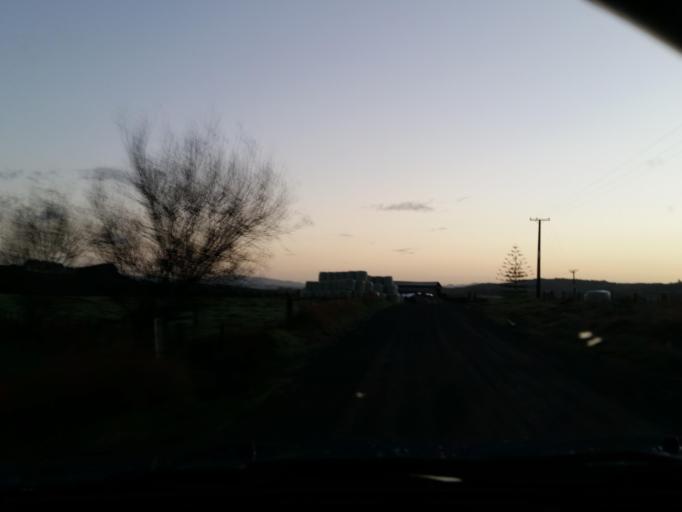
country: NZ
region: Northland
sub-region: Whangarei
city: Maungatapere
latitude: -35.8035
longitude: 174.0493
